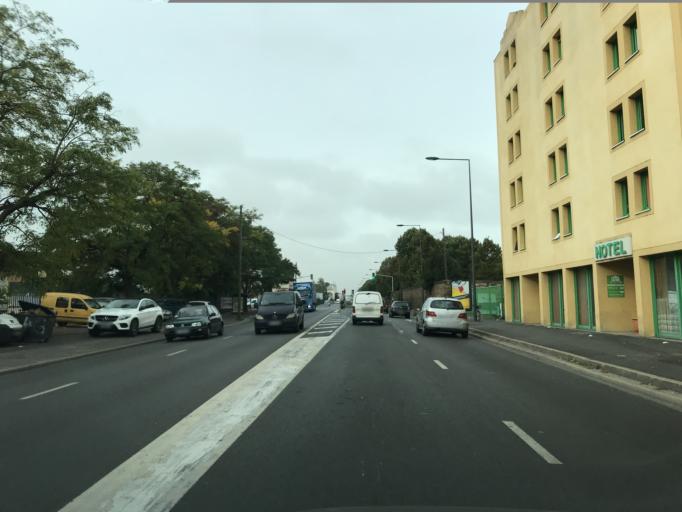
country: FR
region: Ile-de-France
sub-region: Departement de Seine-Saint-Denis
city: Pantin
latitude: 48.9069
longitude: 2.4242
